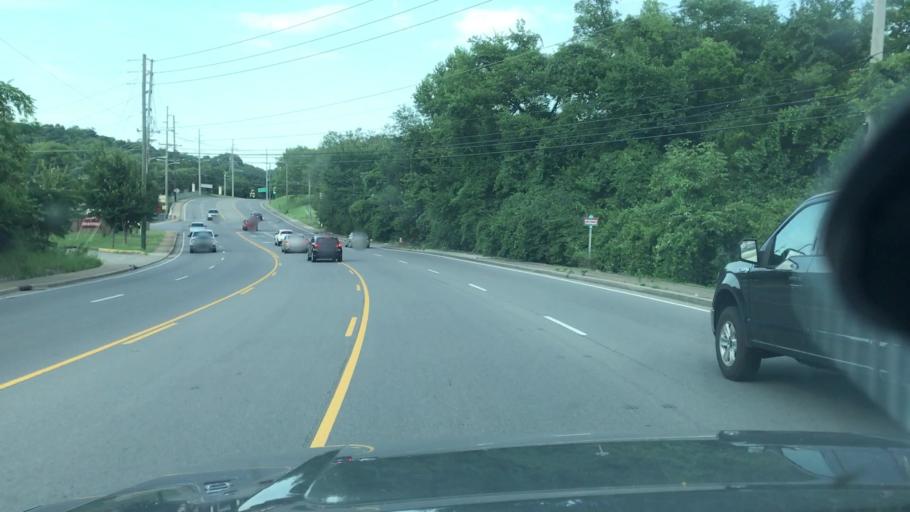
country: US
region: Tennessee
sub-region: Davidson County
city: Nashville
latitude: 36.2016
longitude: -86.8214
